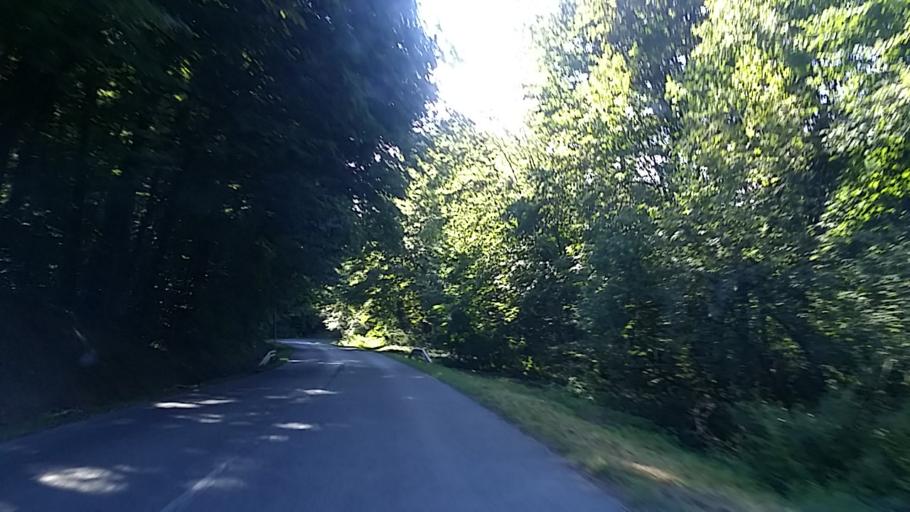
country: HU
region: Baranya
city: Pellerd
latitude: 46.1364
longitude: 18.1431
